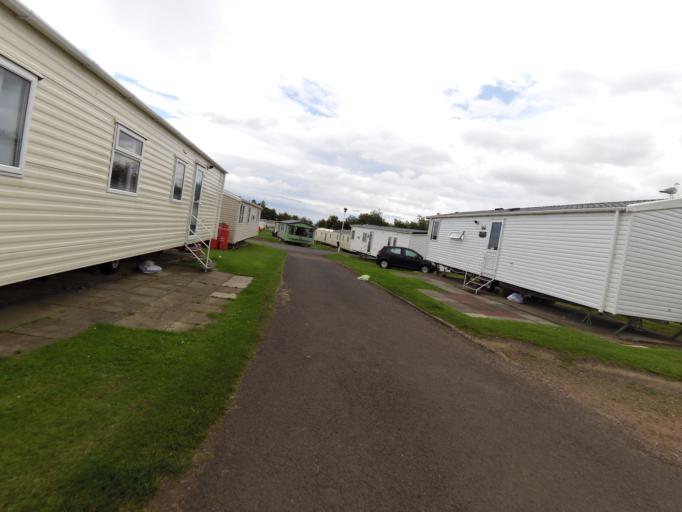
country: GB
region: Scotland
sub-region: East Lothian
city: Cockenzie
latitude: 55.9694
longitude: -2.9354
